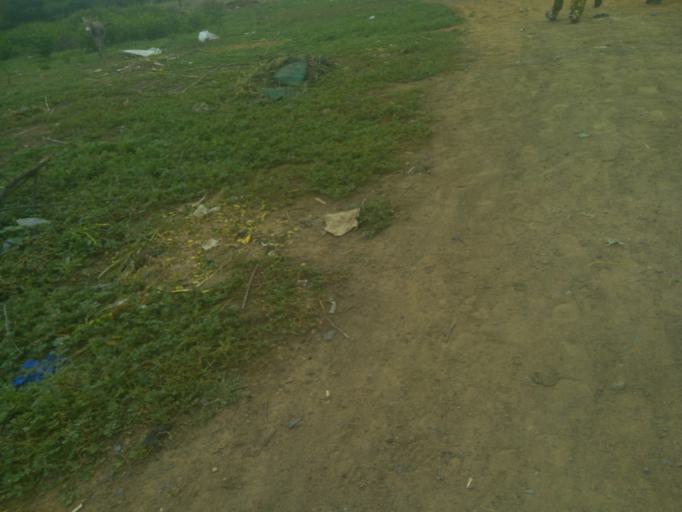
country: ML
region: Kayes
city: Yelimane
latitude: 14.6438
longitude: -10.6960
